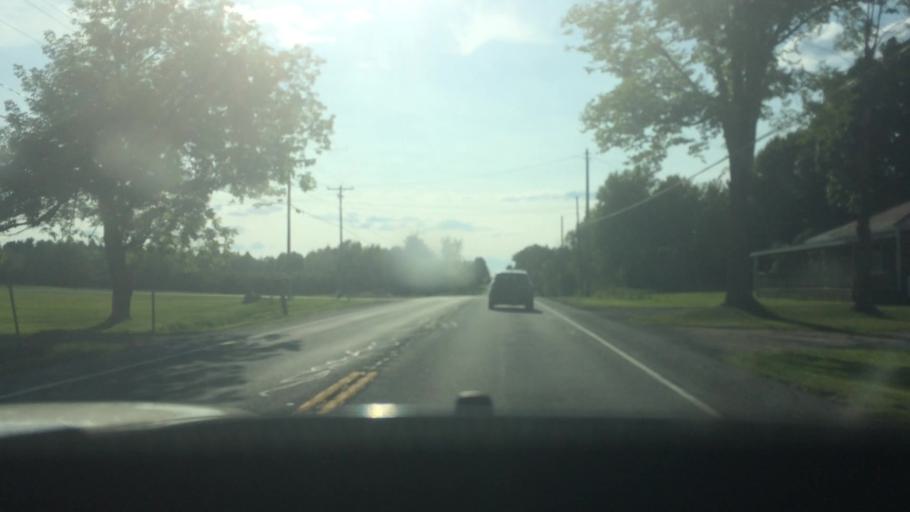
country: US
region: New York
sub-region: St. Lawrence County
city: Potsdam
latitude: 44.6702
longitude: -74.9264
